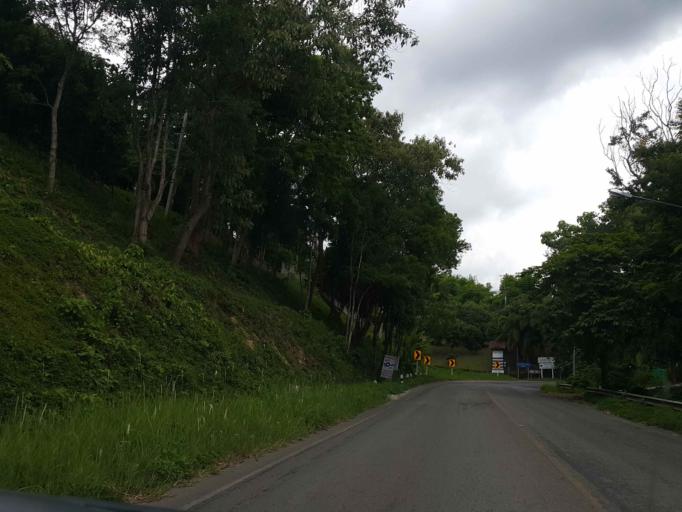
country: TH
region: Chiang Mai
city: Hang Dong
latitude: 18.7857
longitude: 98.8425
